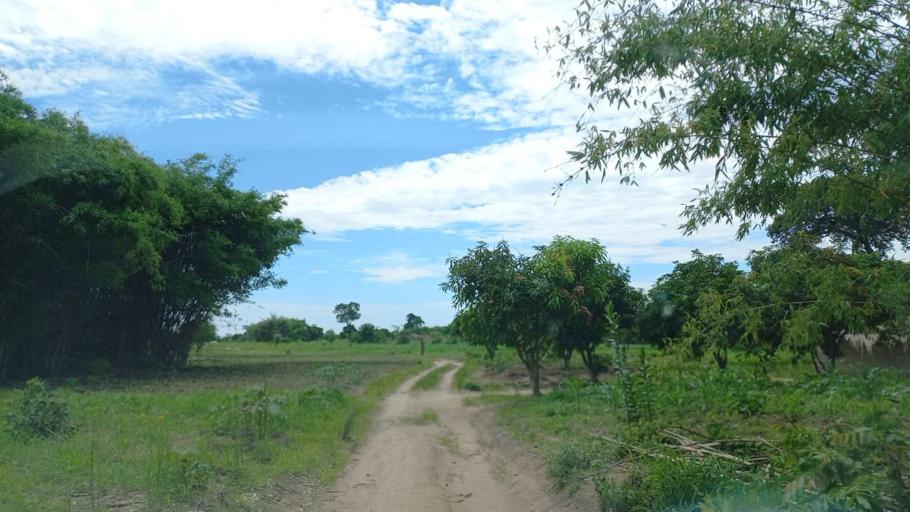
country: ZM
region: Copperbelt
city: Kitwe
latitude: -12.7926
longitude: 28.3992
